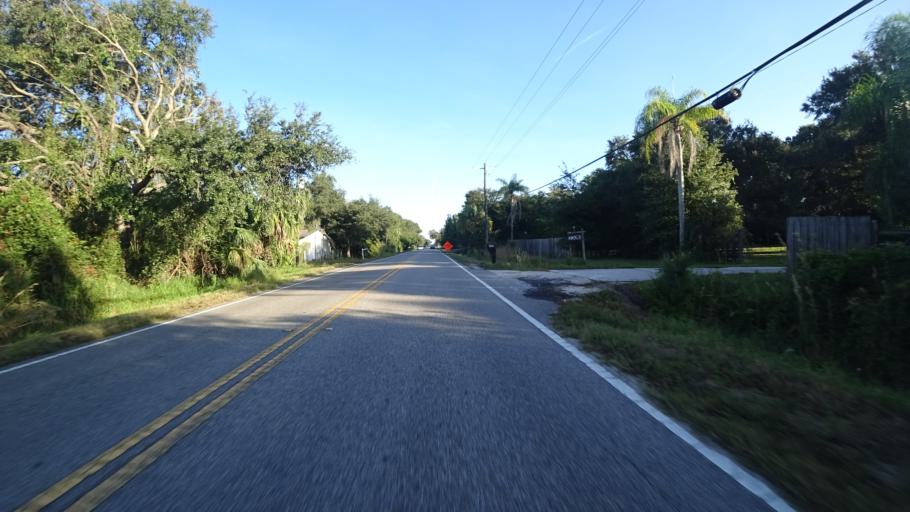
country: US
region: Florida
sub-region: Manatee County
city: Ellenton
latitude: 27.5435
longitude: -82.5283
